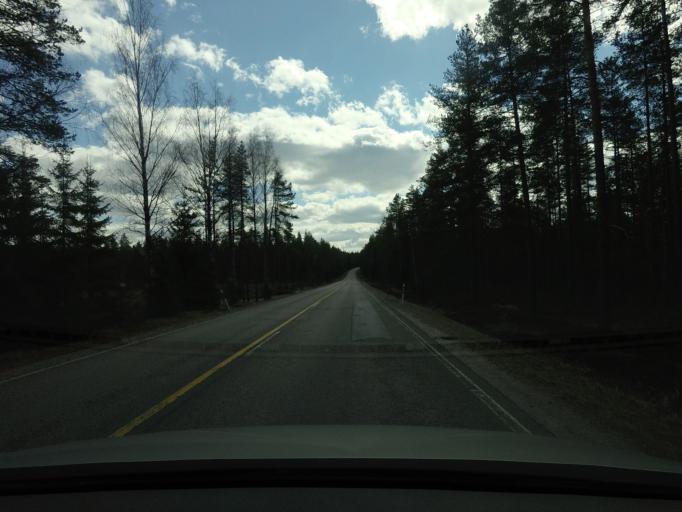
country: FI
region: Kymenlaakso
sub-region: Kotka-Hamina
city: Hamina
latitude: 60.7660
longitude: 27.3467
